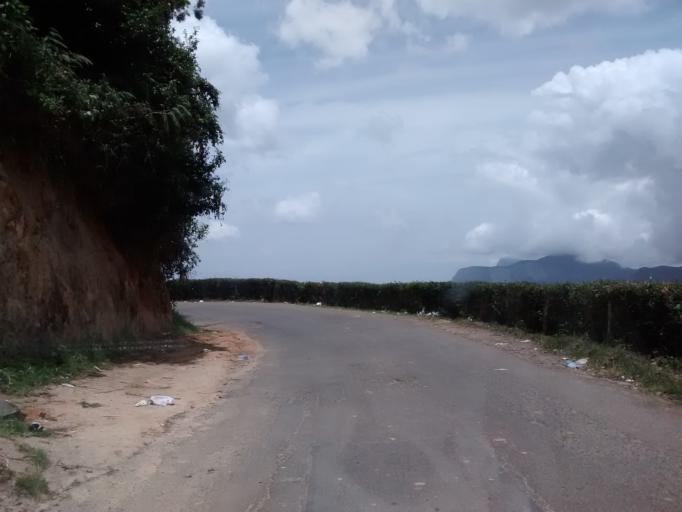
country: IN
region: Tamil Nadu
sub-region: Theni
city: Bodinayakkanur
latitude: 10.1280
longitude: 77.2368
